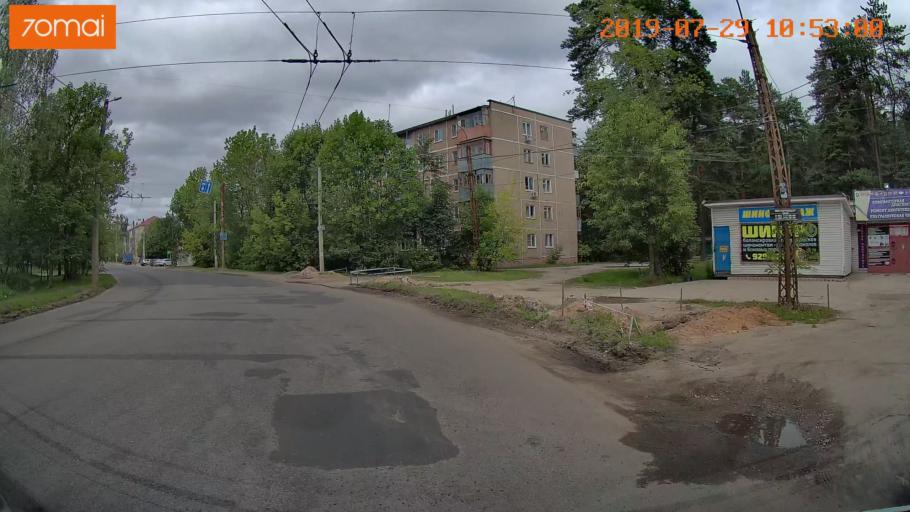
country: RU
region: Ivanovo
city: Kokhma
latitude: 56.9731
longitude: 41.0546
